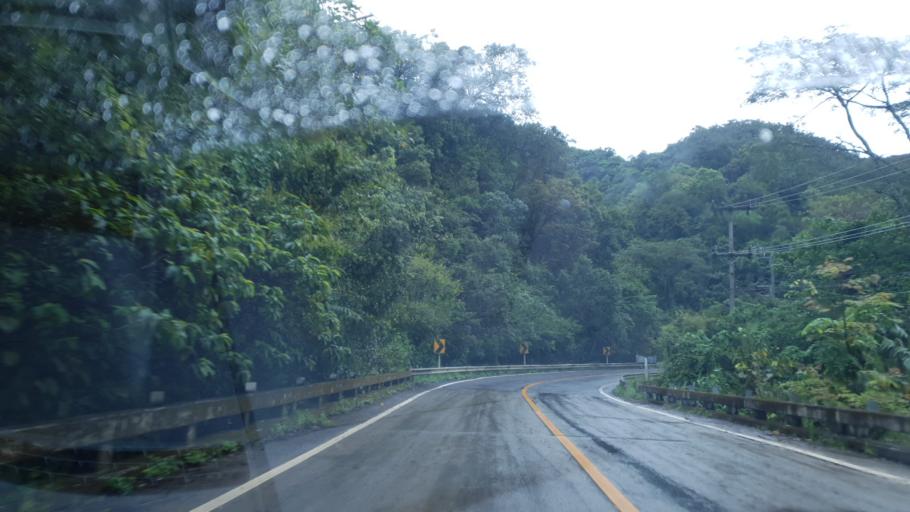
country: TH
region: Mae Hong Son
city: Ban Huai I Huak
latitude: 18.1406
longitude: 98.0857
